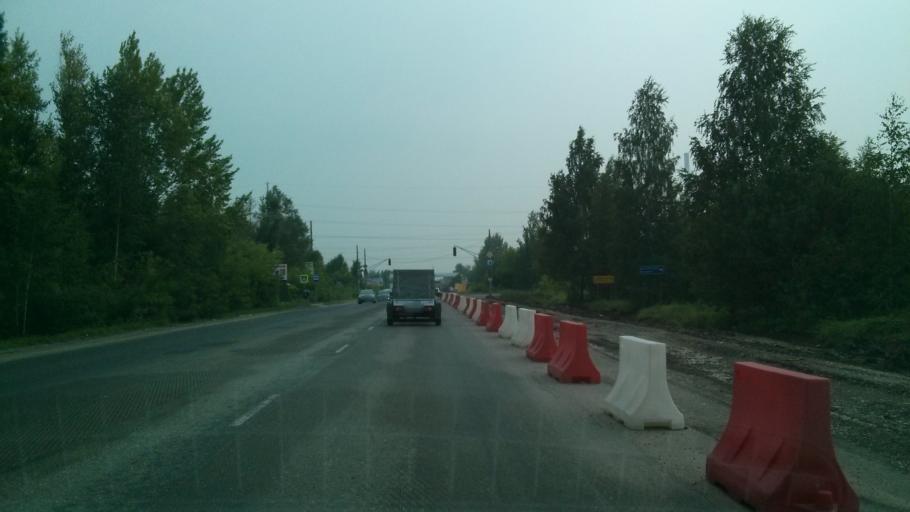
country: RU
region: Nizjnij Novgorod
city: Kstovo
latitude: 56.1180
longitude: 44.1535
